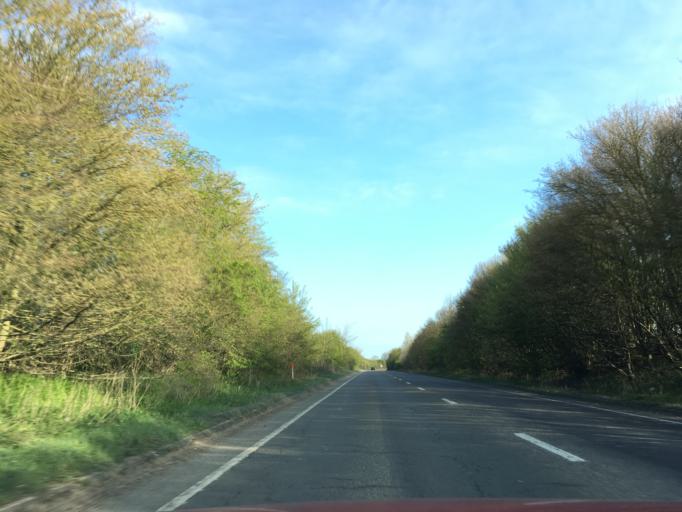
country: GB
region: England
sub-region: Milton Keynes
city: Stony Stratford
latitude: 52.0596
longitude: -0.8709
